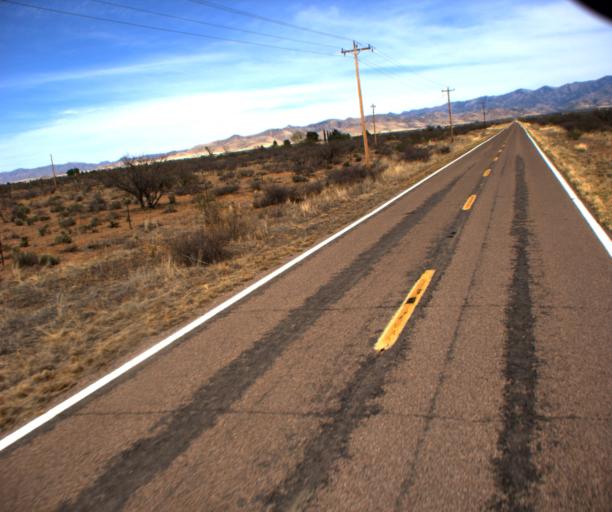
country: US
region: Arizona
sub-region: Cochise County
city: Willcox
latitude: 31.8760
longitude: -109.5522
